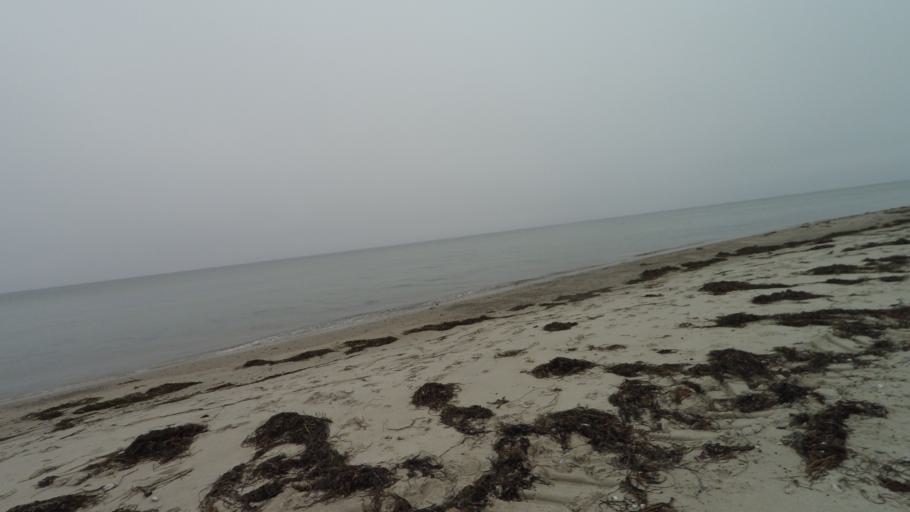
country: DK
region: Central Jutland
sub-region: Arhus Kommune
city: Malling
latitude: 55.9494
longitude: 10.2619
